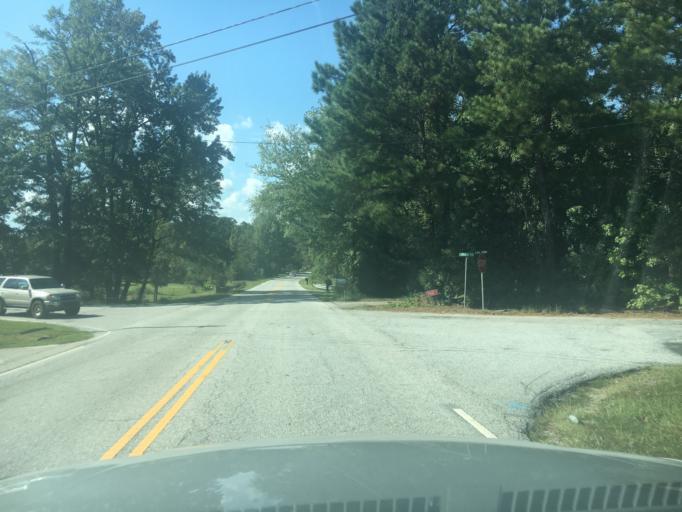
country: US
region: South Carolina
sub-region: Greenwood County
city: Ware Shoals
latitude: 34.2974
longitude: -82.2187
